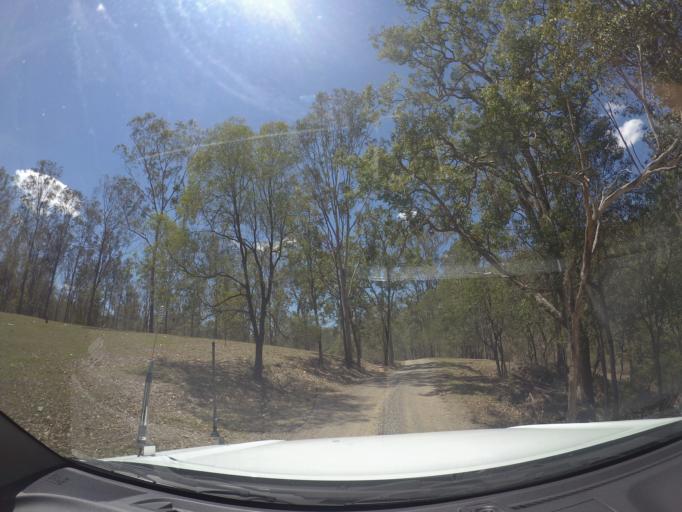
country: AU
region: Queensland
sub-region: Ipswich
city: Deebing Heights
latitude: -27.7606
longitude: 152.8096
